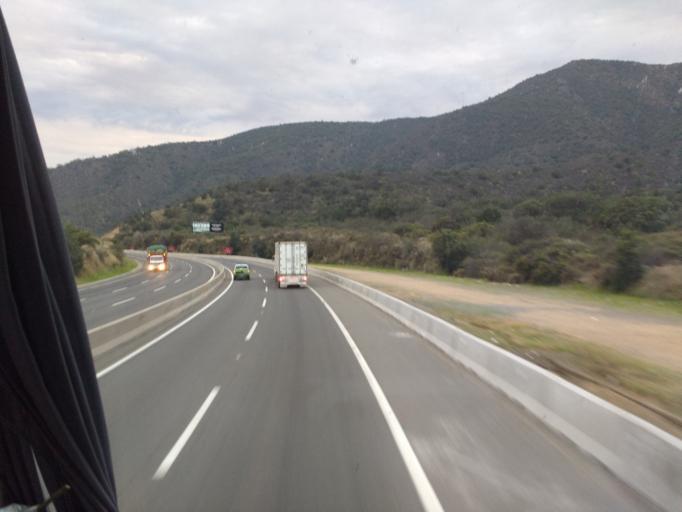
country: CL
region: Santiago Metropolitan
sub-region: Provincia de Chacabuco
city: Lampa
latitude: -33.4439
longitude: -70.9823
